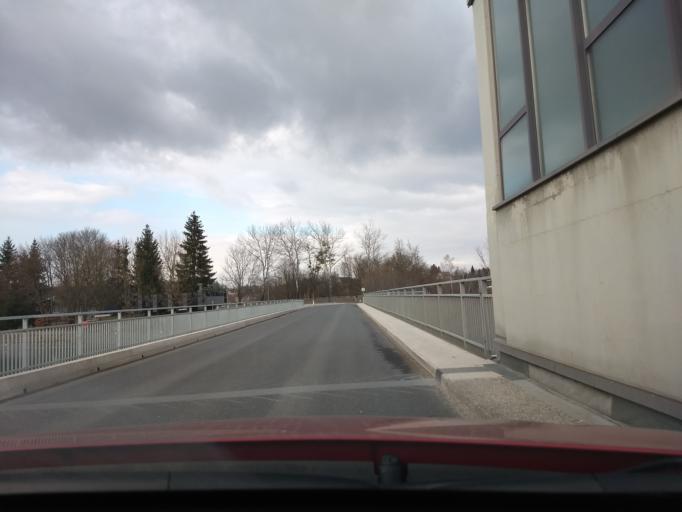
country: AT
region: Upper Austria
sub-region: Politischer Bezirk Steyr-Land
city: Garsten
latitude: 48.0182
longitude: 14.4117
